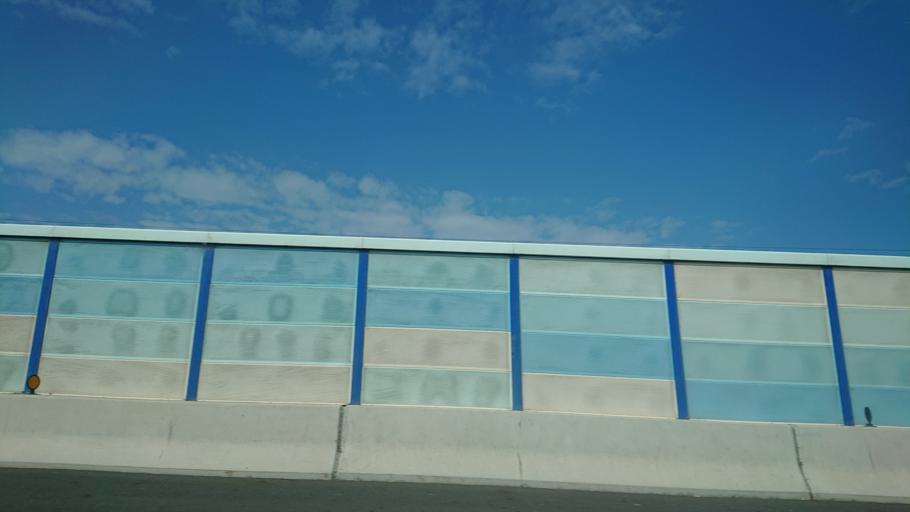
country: TW
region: Taiwan
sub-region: Changhua
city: Chang-hua
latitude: 23.9523
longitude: 120.3298
